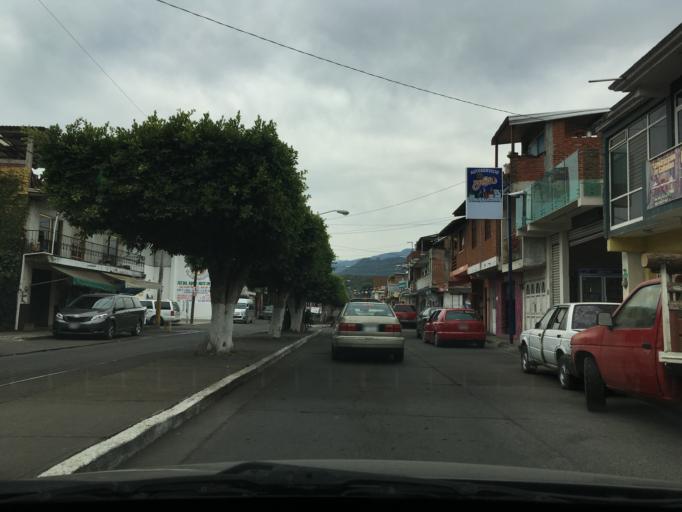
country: MX
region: Michoacan
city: Nuevo San Juan Parangaricutiro
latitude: 19.4157
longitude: -102.1253
